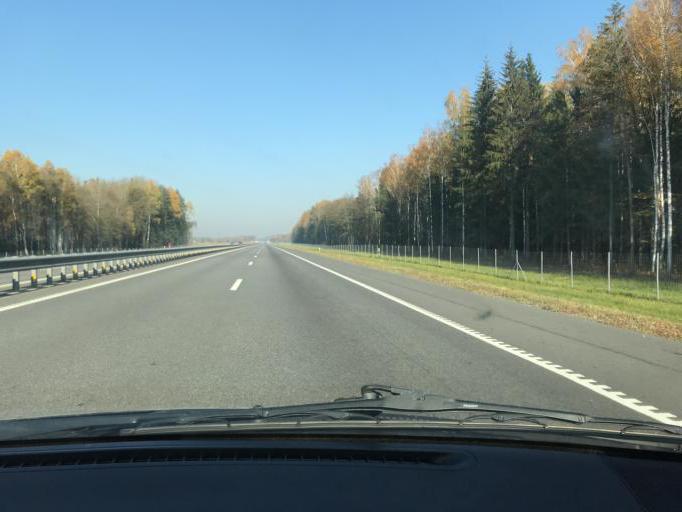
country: BY
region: Minsk
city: Slutsk
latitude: 53.2584
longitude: 27.5503
